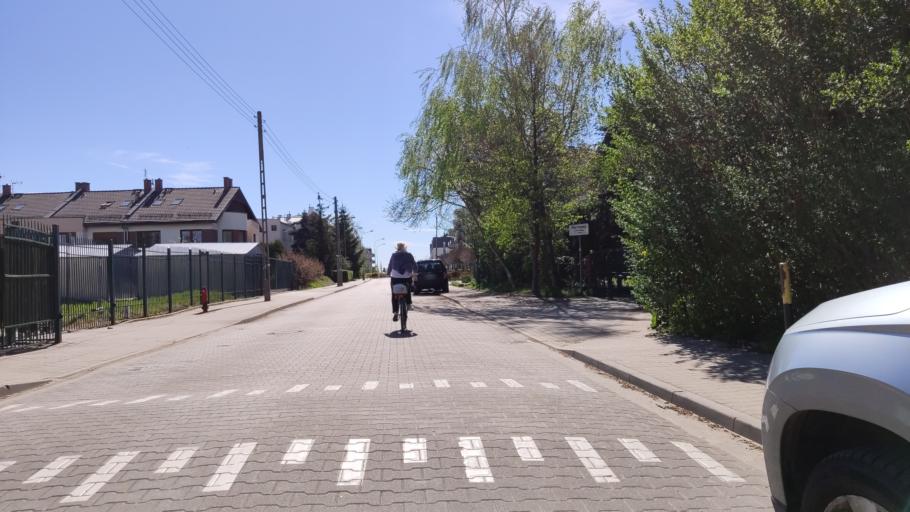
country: PL
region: Lower Silesian Voivodeship
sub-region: Powiat wroclawski
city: Zerniki Wroclawskie
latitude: 51.0626
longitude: 17.0410
